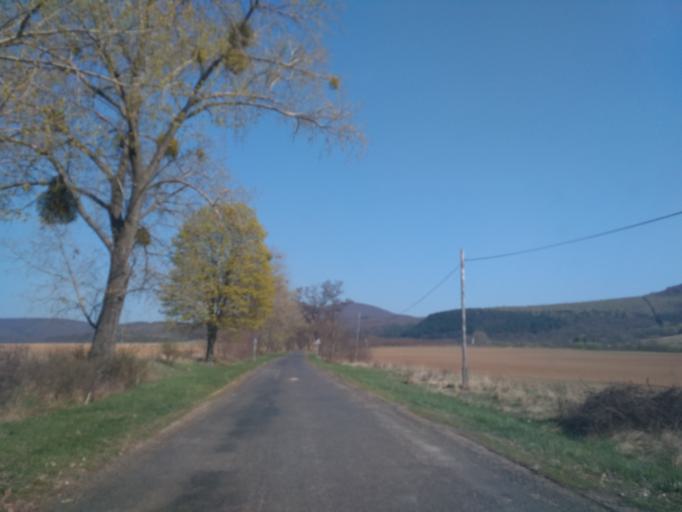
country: HU
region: Borsod-Abauj-Zemplen
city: Gonc
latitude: 48.5323
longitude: 21.3325
